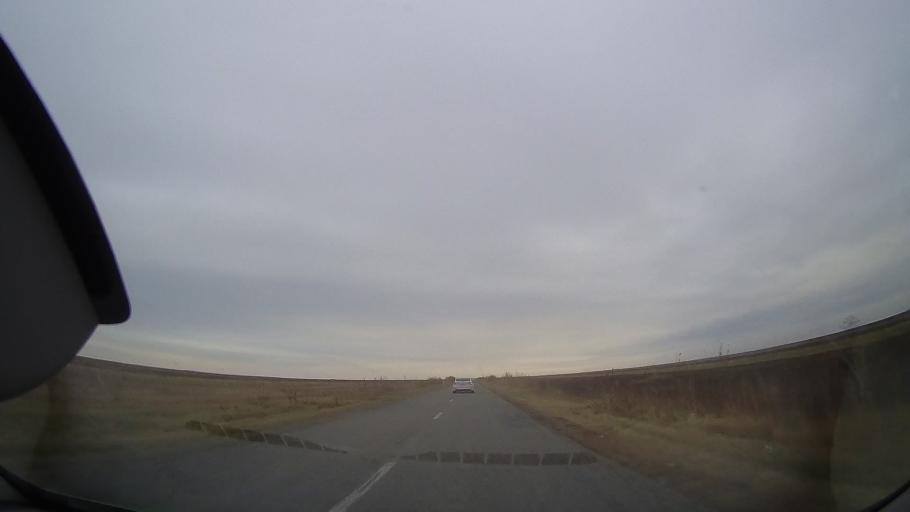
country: RO
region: Ialomita
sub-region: Oras Amara
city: Amara
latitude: 44.6606
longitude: 27.3007
